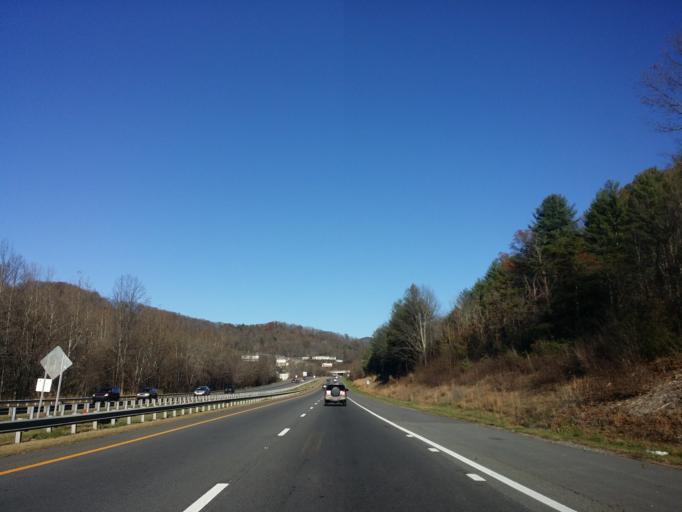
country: US
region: North Carolina
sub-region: Buncombe County
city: Swannanoa
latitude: 35.5844
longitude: -82.4579
